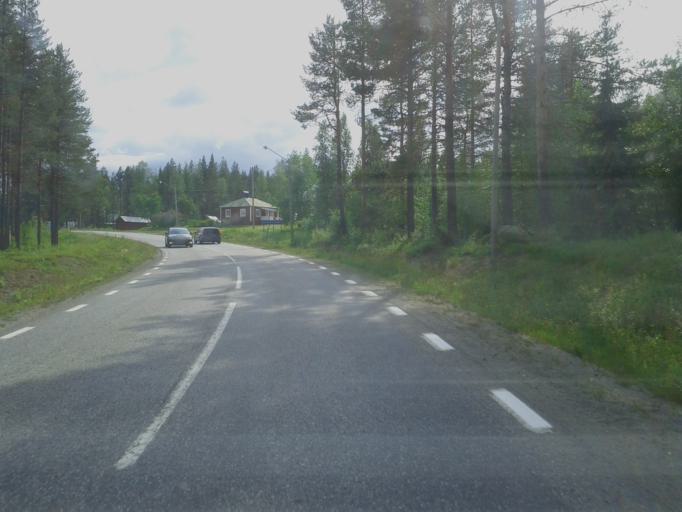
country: SE
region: Vaesterbotten
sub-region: Sorsele Kommun
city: Sorsele
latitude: 65.2428
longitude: 17.6629
